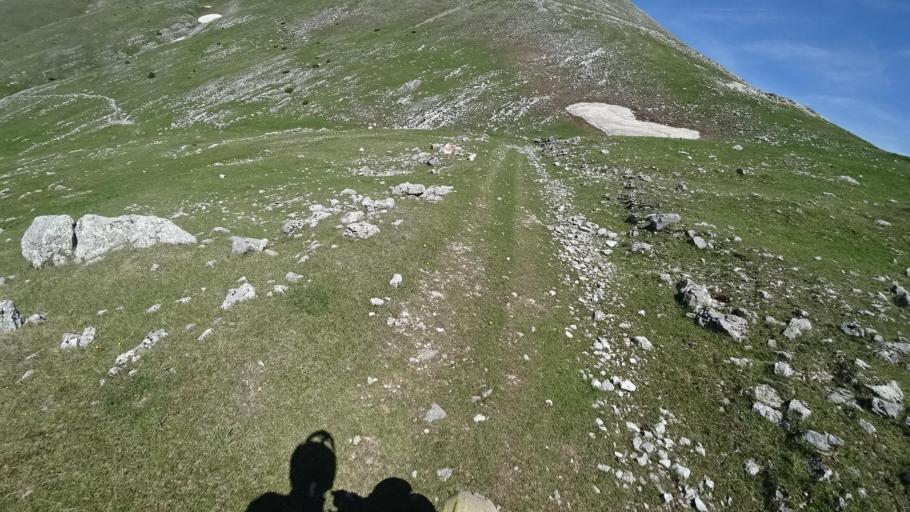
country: BA
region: Federation of Bosnia and Herzegovina
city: Gracanica
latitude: 43.6927
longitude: 18.2665
